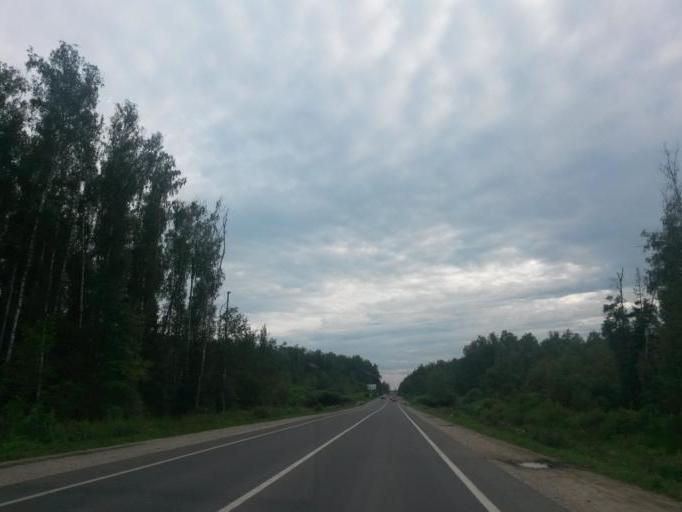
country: RU
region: Moskovskaya
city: Vostryakovo
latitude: 55.4243
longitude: 37.8475
